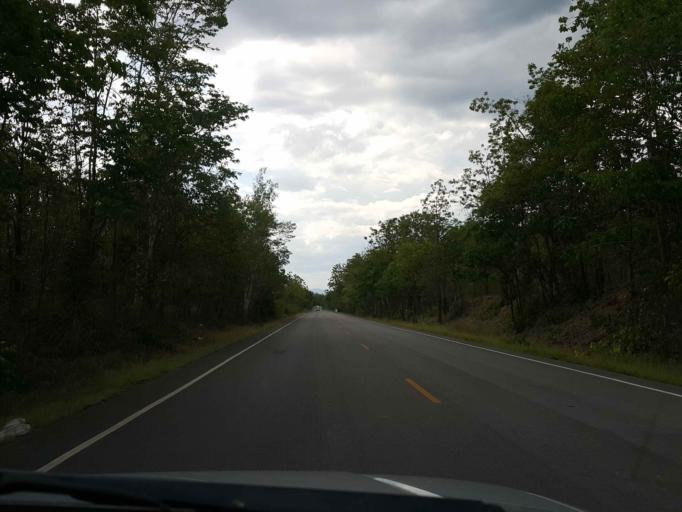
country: TH
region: Sukhothai
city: Thung Saliam
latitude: 17.3712
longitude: 99.4051
